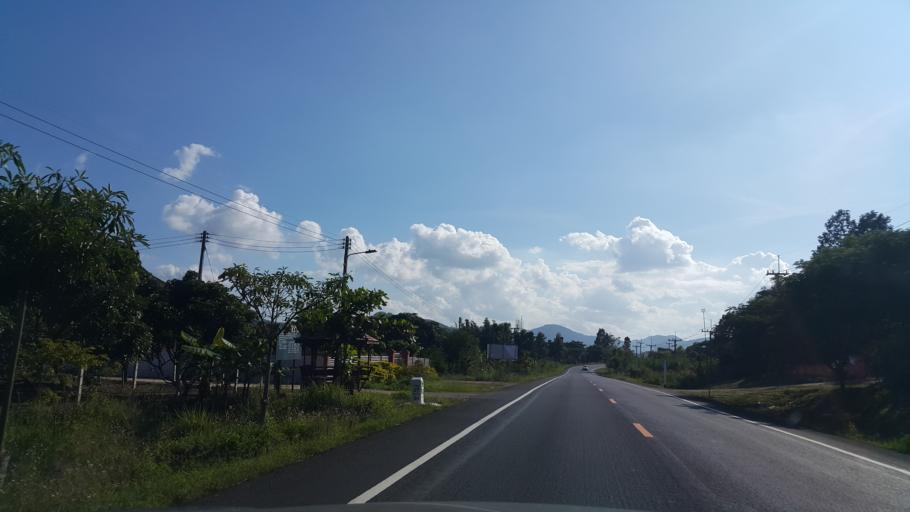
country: TH
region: Lamphun
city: Mae Tha
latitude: 18.4845
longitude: 99.1795
